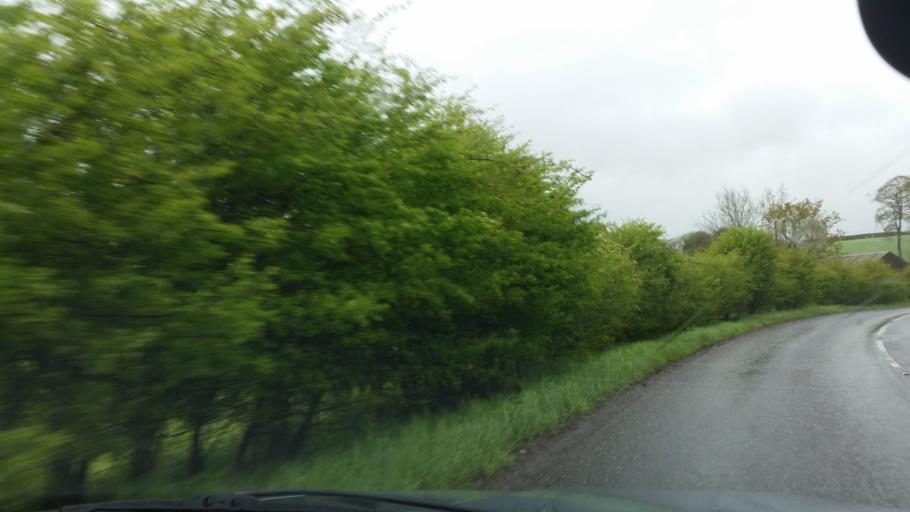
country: GB
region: Northern Ireland
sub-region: Omagh District
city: Omagh
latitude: 54.5726
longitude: -7.2776
